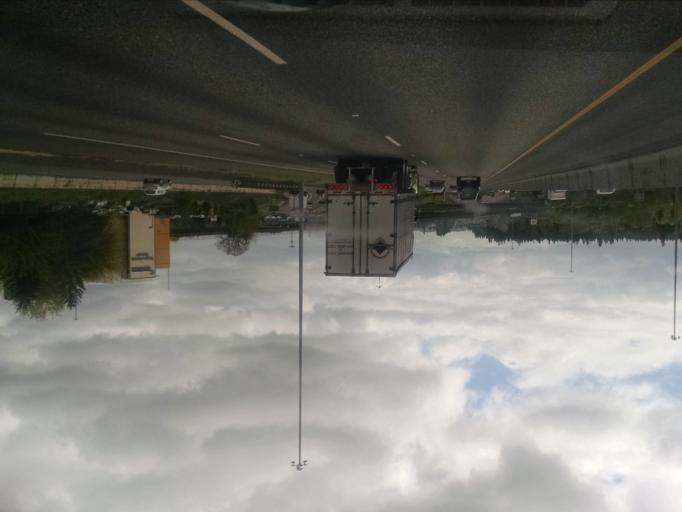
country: US
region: Oregon
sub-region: Washington County
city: Durham
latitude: 45.4244
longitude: -122.7442
